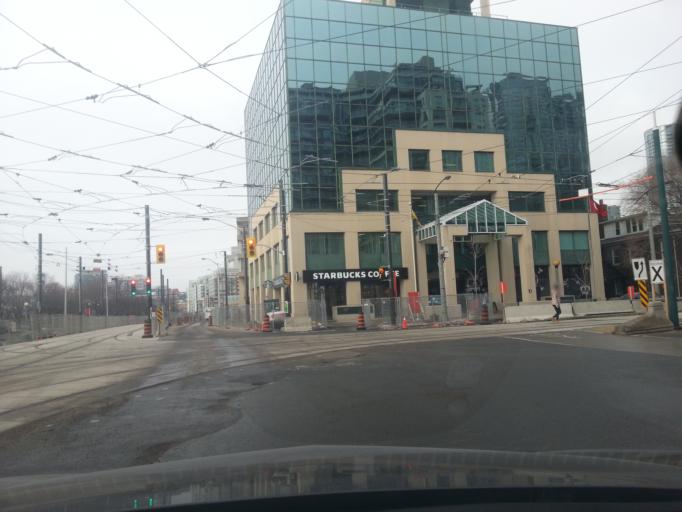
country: CA
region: Ontario
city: Toronto
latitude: 43.6378
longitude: -79.3917
